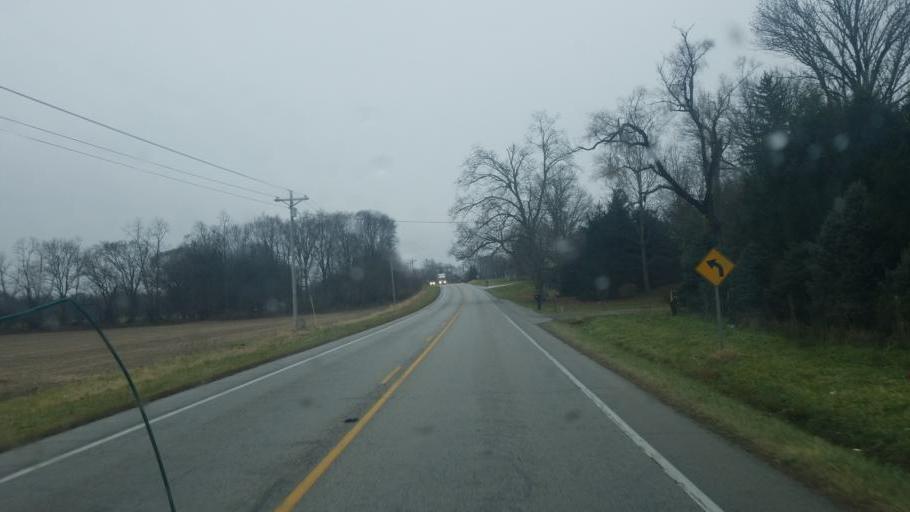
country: US
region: Indiana
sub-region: Shelby County
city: Shelbyville
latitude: 39.5712
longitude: -85.7766
